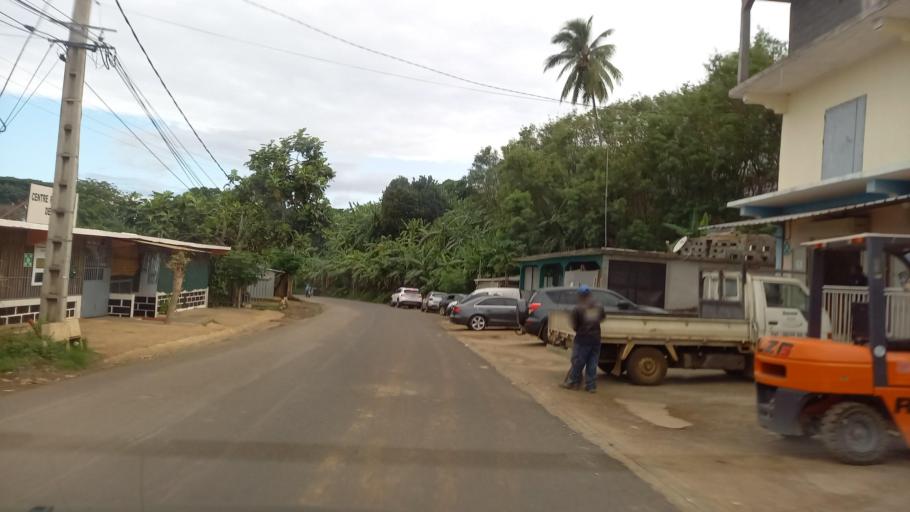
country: YT
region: Sada
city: Sada
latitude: -12.8503
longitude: 45.1047
